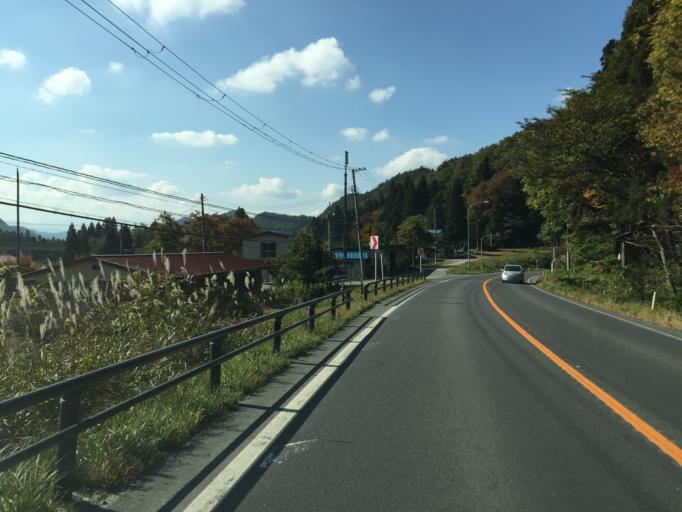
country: JP
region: Yamagata
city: Yonezawa
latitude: 37.8716
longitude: 140.2088
